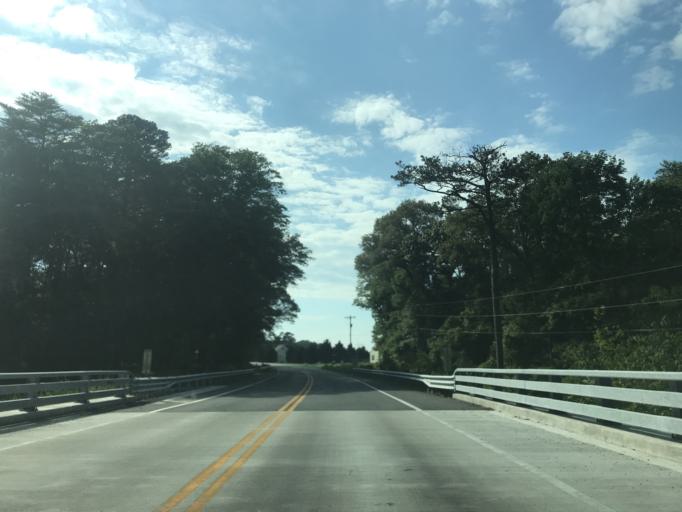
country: US
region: Maryland
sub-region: Wicomico County
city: Hebron
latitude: 38.4636
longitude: -75.7071
